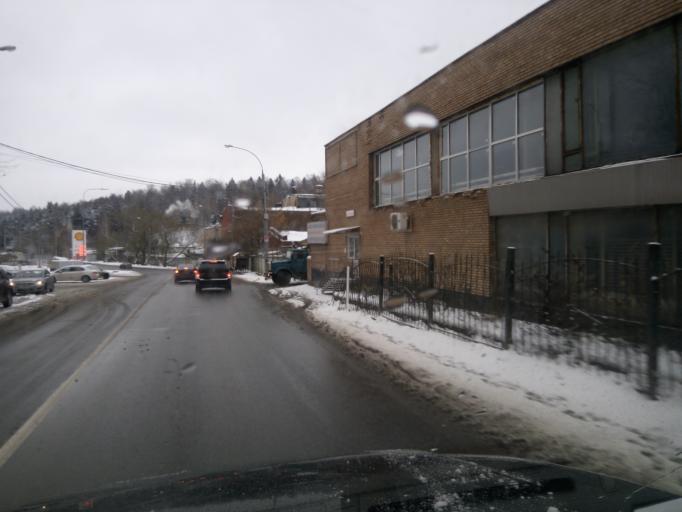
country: RU
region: Moskovskaya
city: Skhodnya
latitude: 55.9612
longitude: 37.3079
